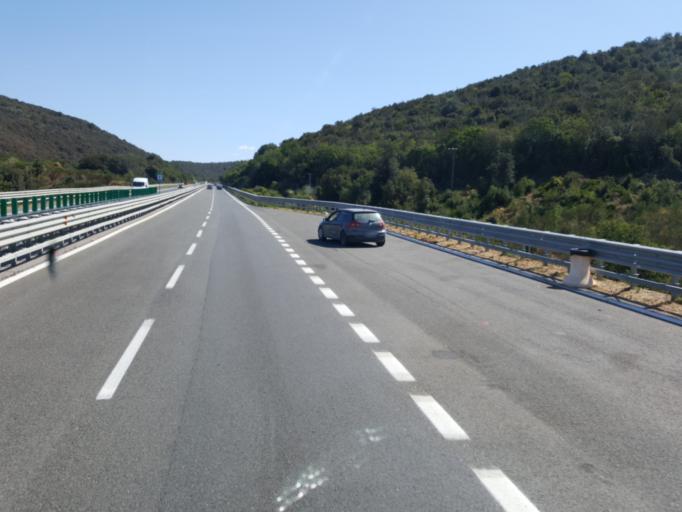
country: IT
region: Tuscany
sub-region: Provincia di Grosseto
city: Bagno Roselle
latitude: 42.8544
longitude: 11.1746
